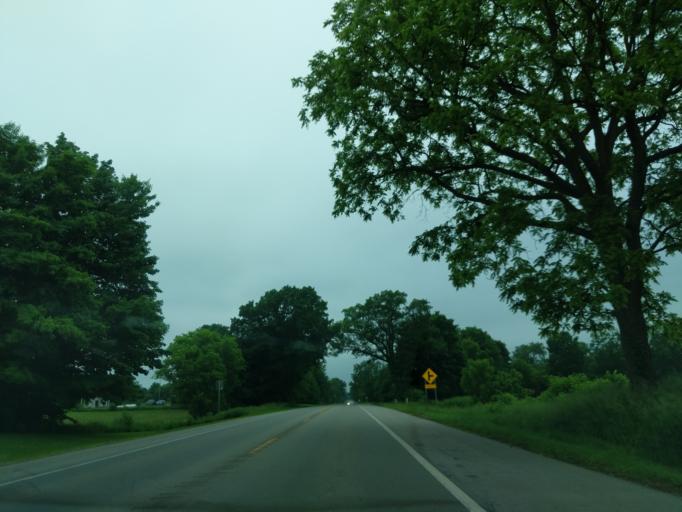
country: US
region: Michigan
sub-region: Branch County
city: Quincy
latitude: 41.9488
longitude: -84.8383
